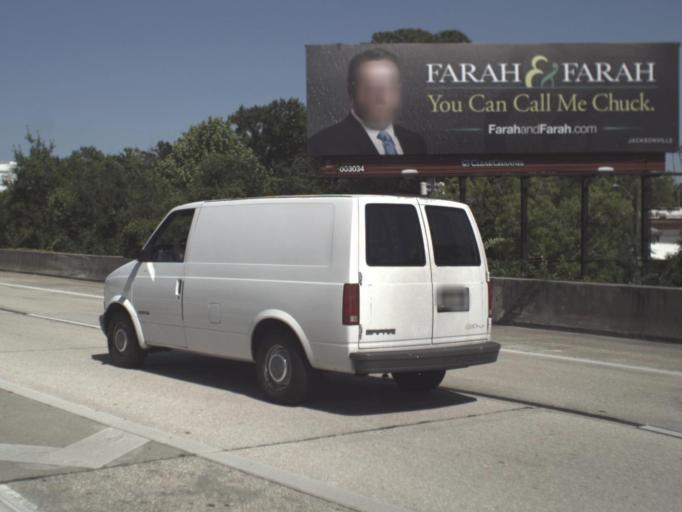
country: US
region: Florida
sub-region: Duval County
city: Jacksonville
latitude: 30.3213
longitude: -81.6985
